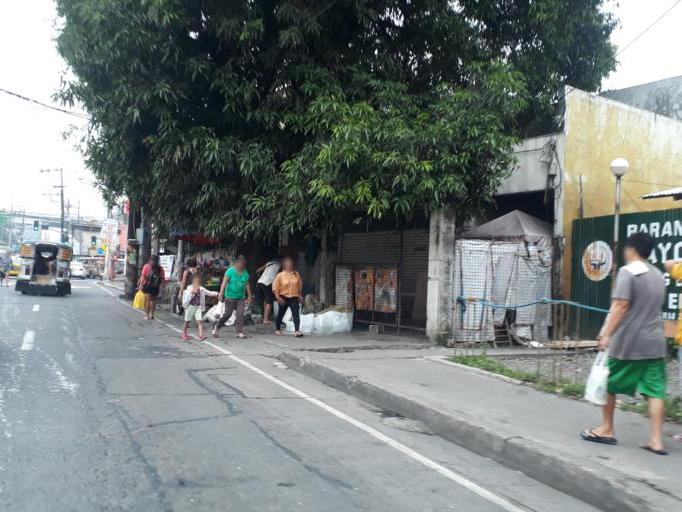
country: PH
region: Metro Manila
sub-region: Caloocan City
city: Niugan
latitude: 14.6579
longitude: 120.9704
